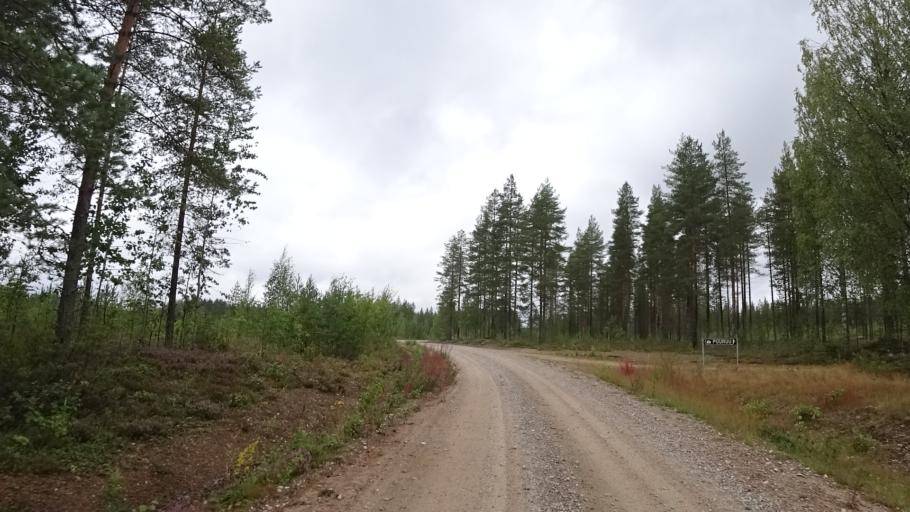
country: FI
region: North Karelia
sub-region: Pielisen Karjala
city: Lieksa
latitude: 63.5190
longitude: 30.1119
